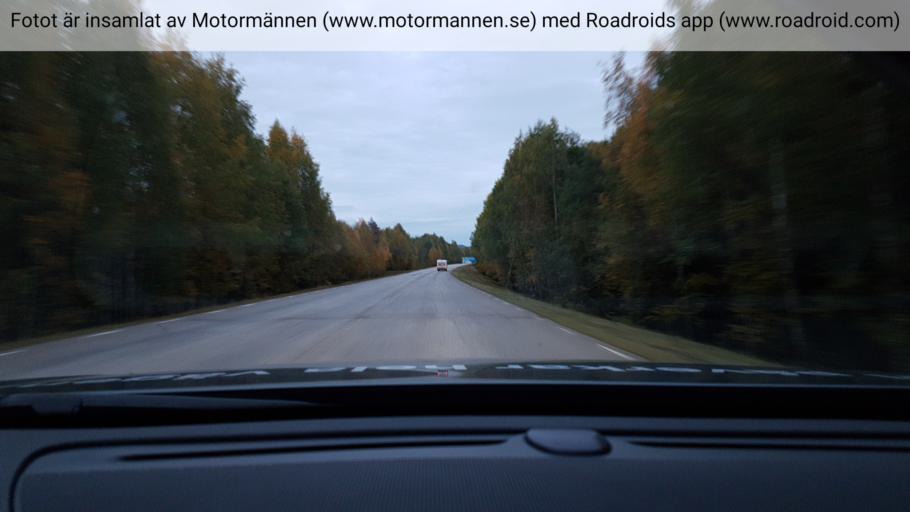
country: SE
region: Norrbotten
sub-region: Alvsbyns Kommun
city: AElvsbyn
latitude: 65.8432
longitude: 20.4932
